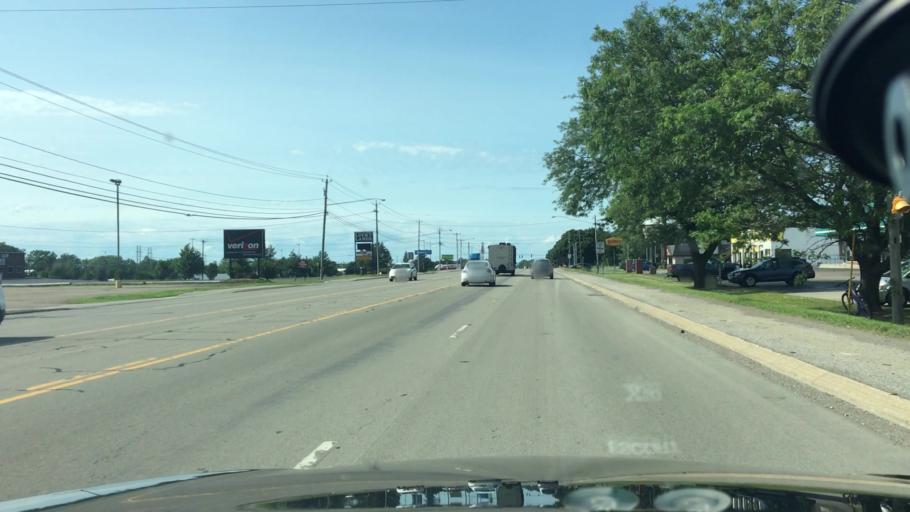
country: US
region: New York
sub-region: Chautauqua County
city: Fredonia
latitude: 42.4522
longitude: -79.3088
